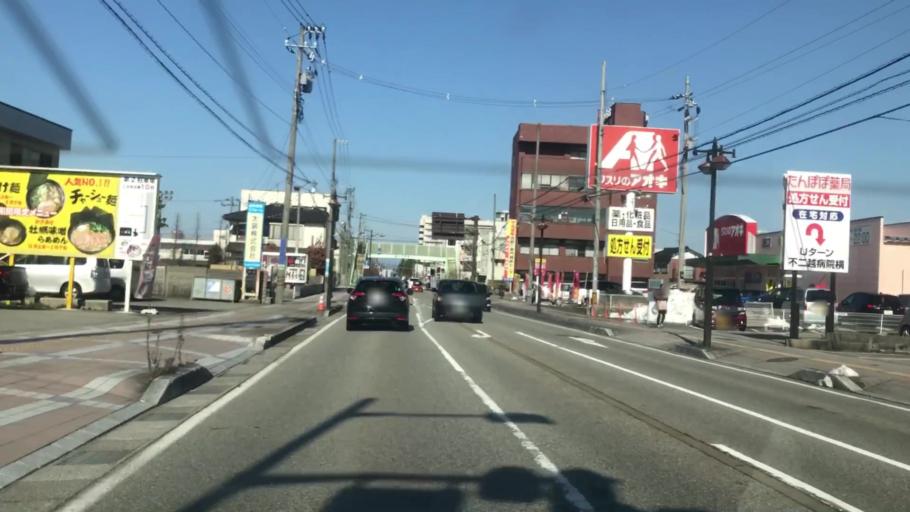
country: JP
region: Toyama
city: Toyama-shi
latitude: 36.6881
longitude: 137.2363
